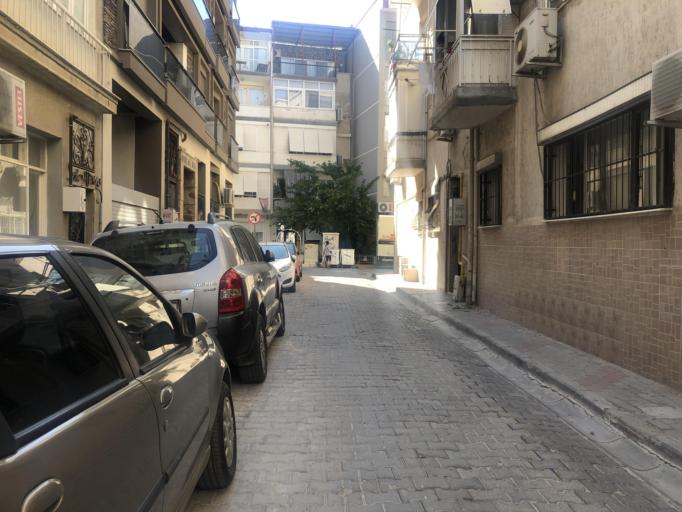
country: TR
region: Izmir
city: Karsiyaka
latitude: 38.4589
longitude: 27.1225
